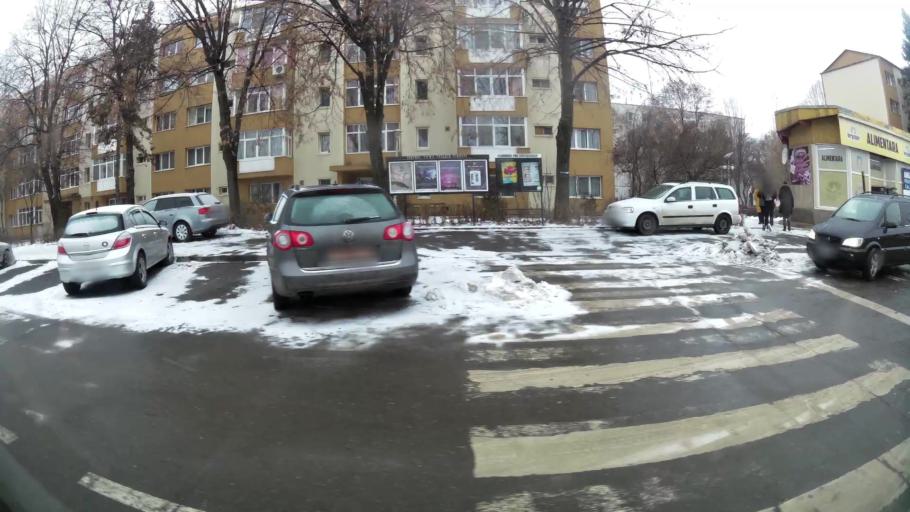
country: RO
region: Prahova
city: Ploiesti
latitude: 44.9601
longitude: 26.0102
